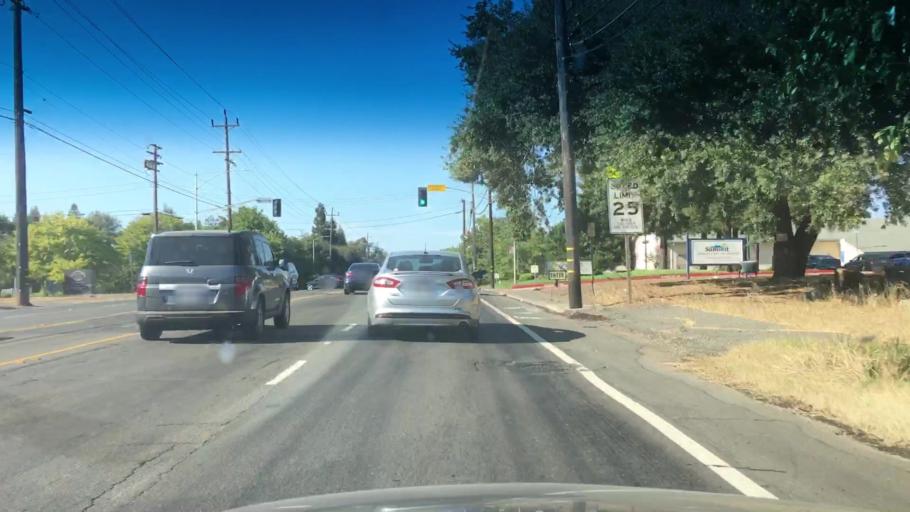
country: US
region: California
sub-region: Sacramento County
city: Orangevale
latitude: 38.6561
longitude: -121.2256
